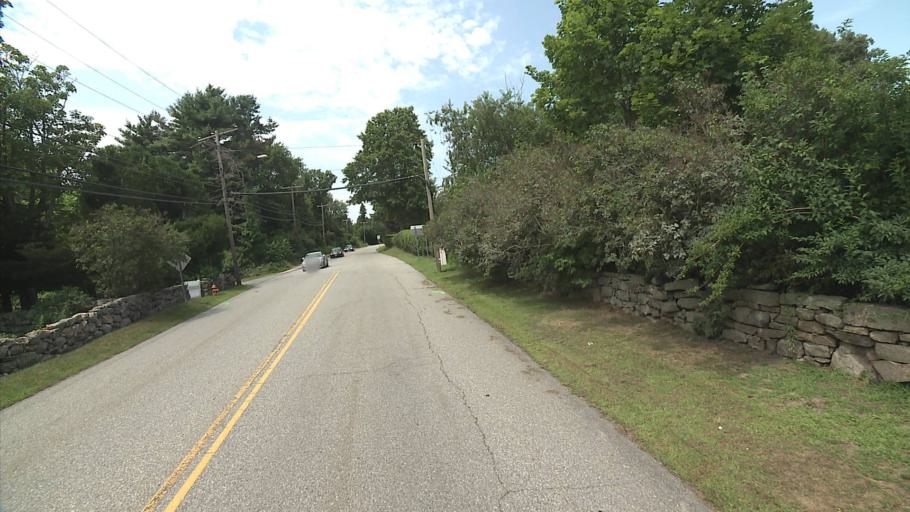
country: US
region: Connecticut
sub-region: New London County
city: Central Waterford
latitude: 41.3057
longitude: -72.1263
